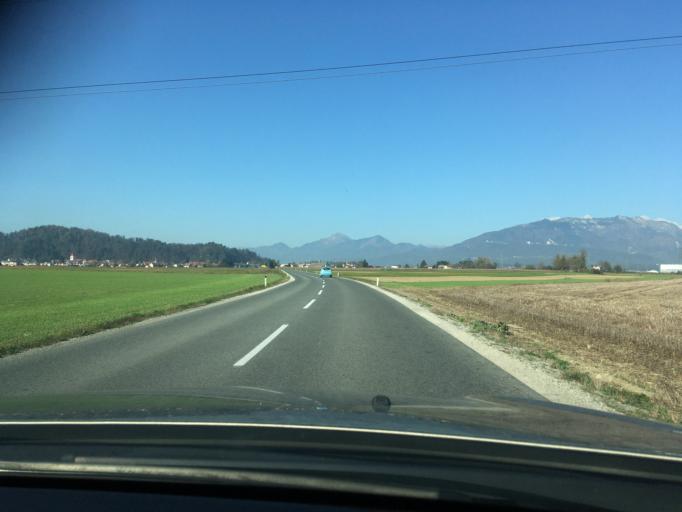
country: SI
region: Menges
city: Menges
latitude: 46.1554
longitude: 14.5863
